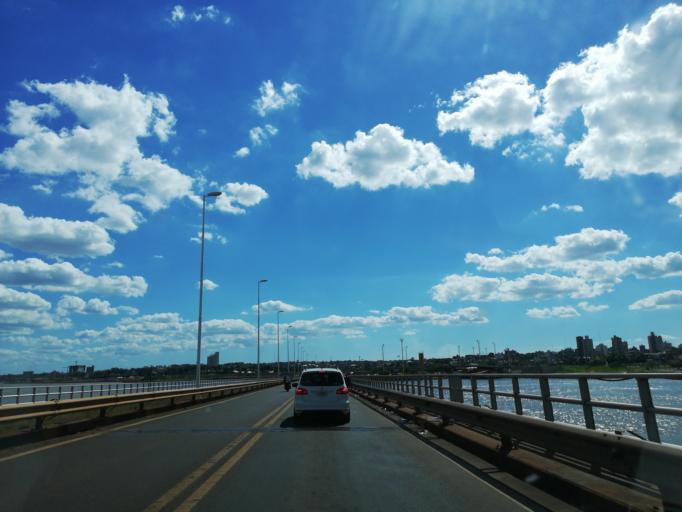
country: AR
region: Misiones
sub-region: Departamento de Capital
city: Posadas
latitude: -27.3752
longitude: -55.8773
